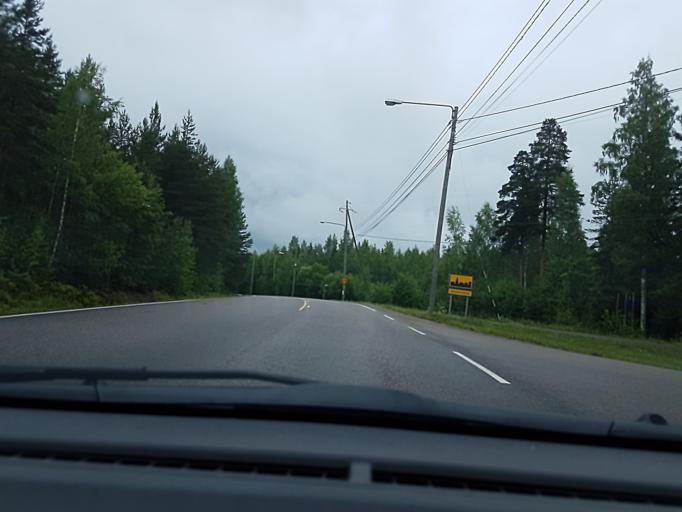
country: FI
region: Uusimaa
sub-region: Helsinki
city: Pornainen
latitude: 60.4643
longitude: 25.3905
